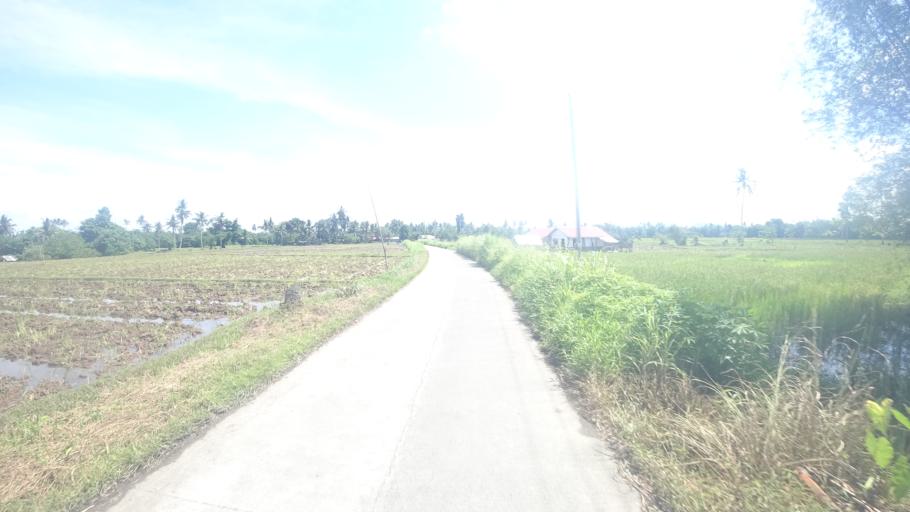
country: PH
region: Eastern Visayas
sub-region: Province of Leyte
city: Alangalang
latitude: 11.2193
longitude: 124.8464
